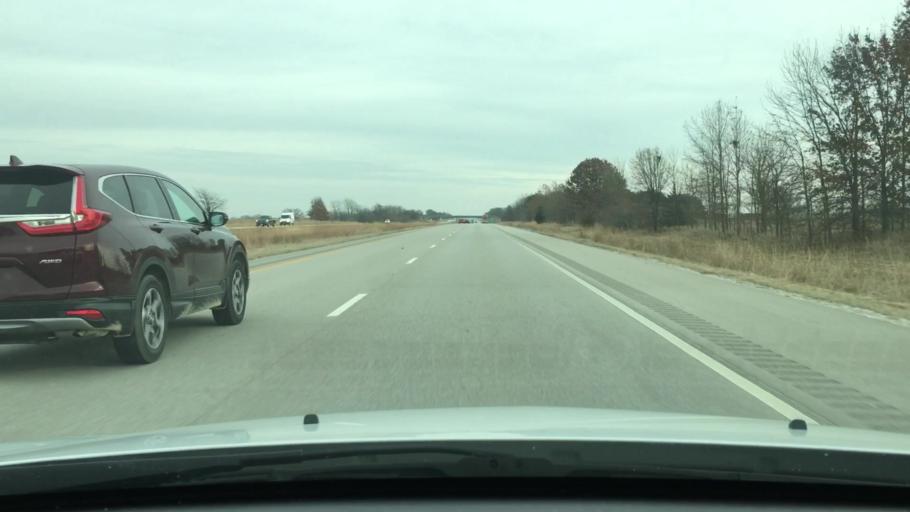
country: US
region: Illinois
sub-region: Sangamon County
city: New Berlin
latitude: 39.7399
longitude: -89.9486
